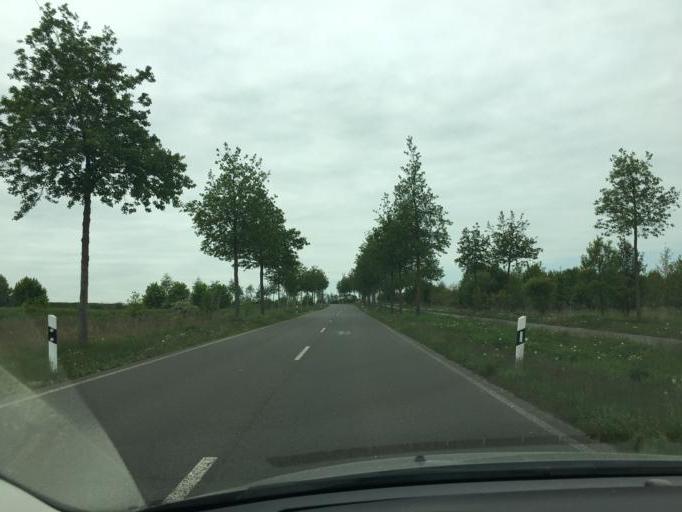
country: DE
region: Saxony
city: Taucha
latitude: 51.3921
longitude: 12.4422
